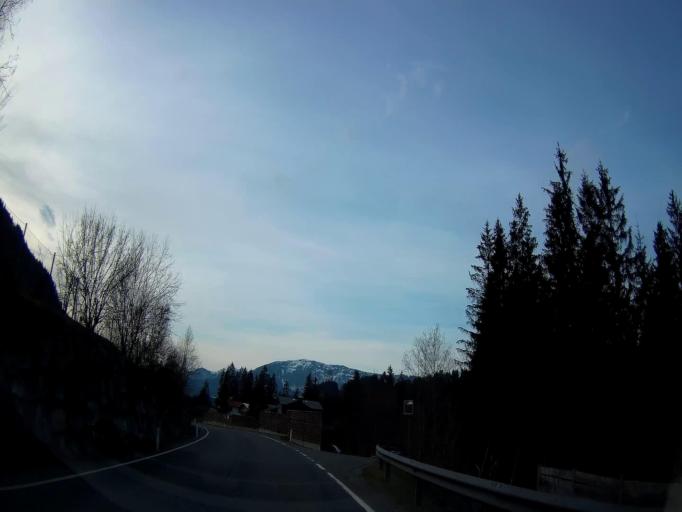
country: AT
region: Salzburg
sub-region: Politischer Bezirk Hallein
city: Abtenau
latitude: 47.5551
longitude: 13.4086
